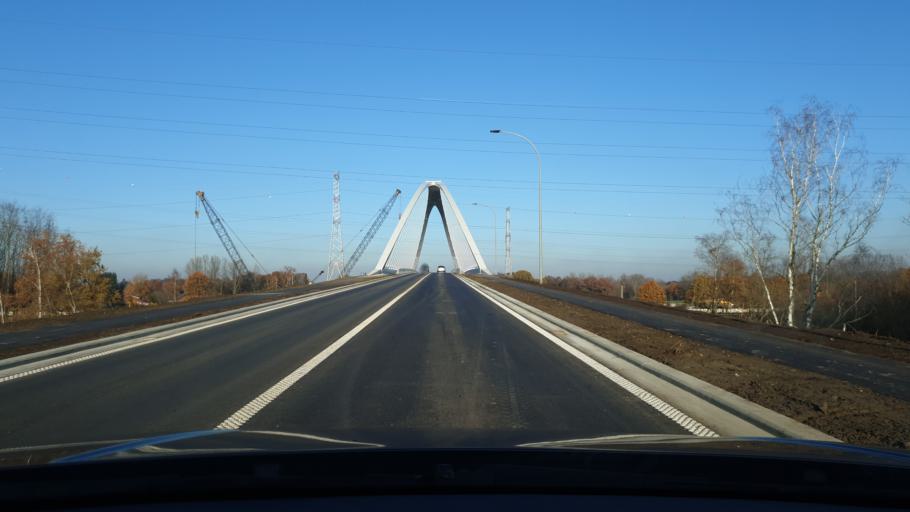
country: BE
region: Flanders
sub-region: Provincie Antwerpen
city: Geel
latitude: 51.1239
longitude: 4.9817
